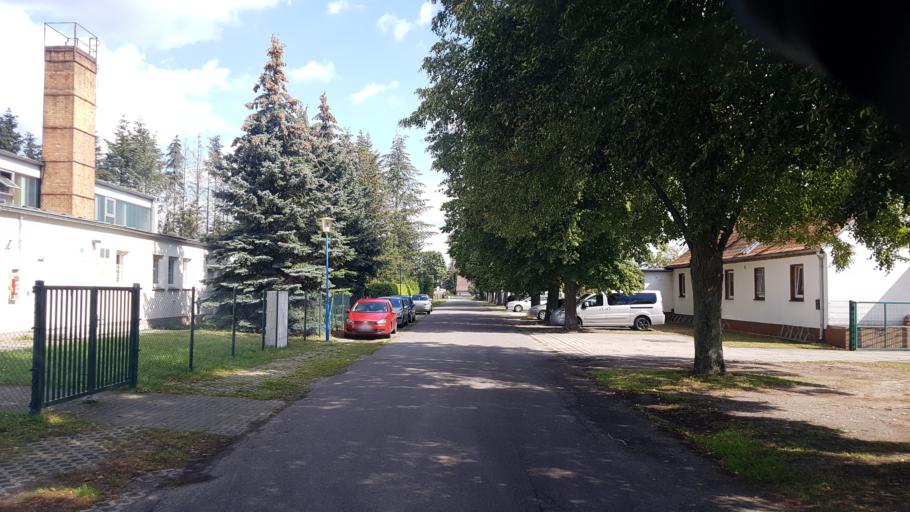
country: DE
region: Brandenburg
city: Spremberg
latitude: 51.6733
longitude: 14.4375
